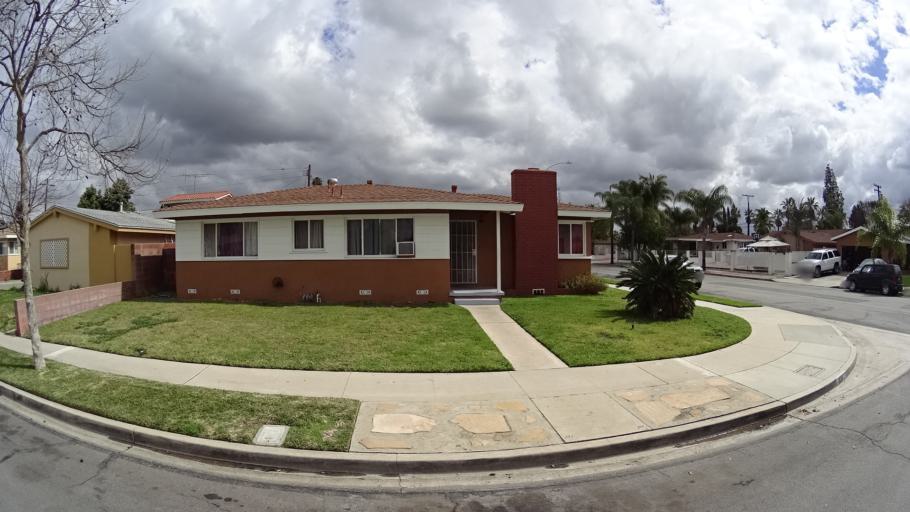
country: US
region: California
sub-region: Orange County
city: Anaheim
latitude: 33.8241
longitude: -117.9301
